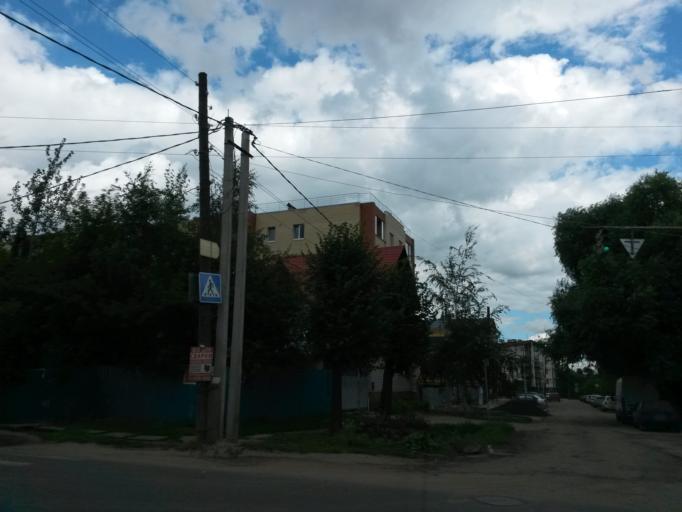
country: RU
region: Jaroslavl
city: Yaroslavl
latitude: 57.6118
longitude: 39.8889
